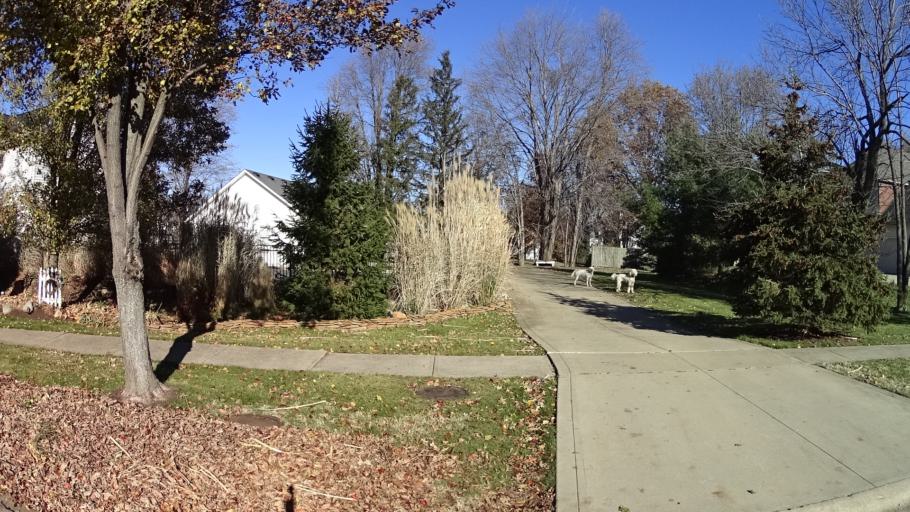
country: US
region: Ohio
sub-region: Lorain County
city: Avon Center
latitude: 41.4846
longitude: -81.9970
